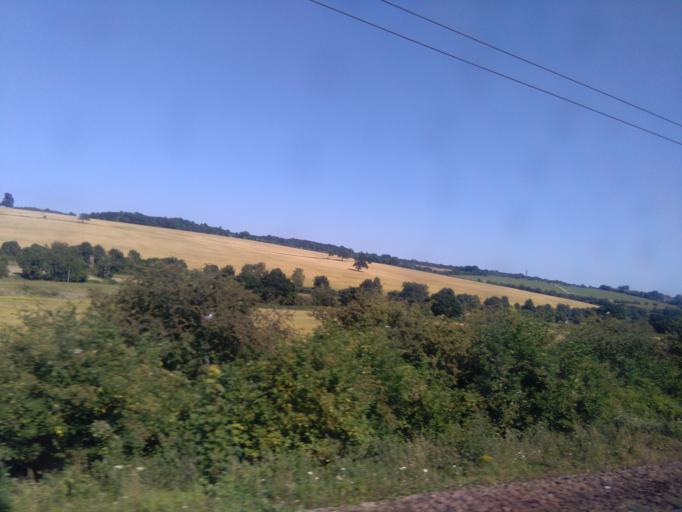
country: GB
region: England
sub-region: Hertfordshire
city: Harpenden
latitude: 51.8350
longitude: -0.3584
